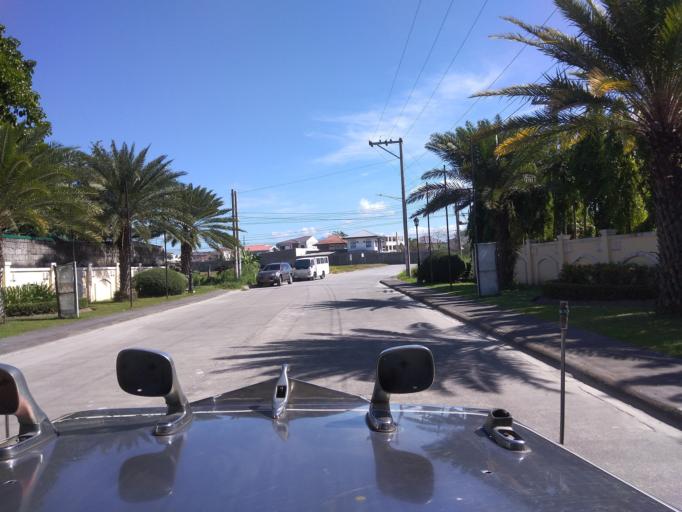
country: PH
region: Central Luzon
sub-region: Province of Pampanga
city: Calibutbut
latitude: 15.1073
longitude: 120.6053
